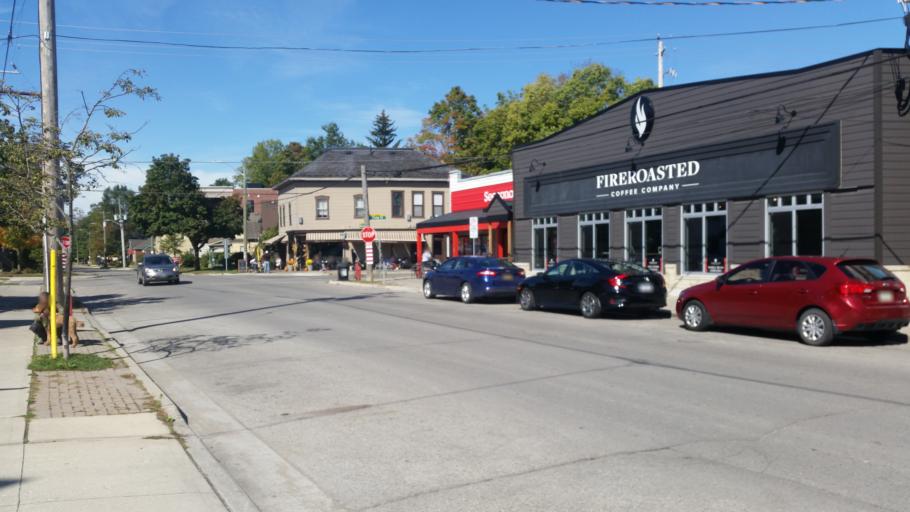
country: CA
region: Ontario
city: London
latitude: 42.9731
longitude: -81.2538
